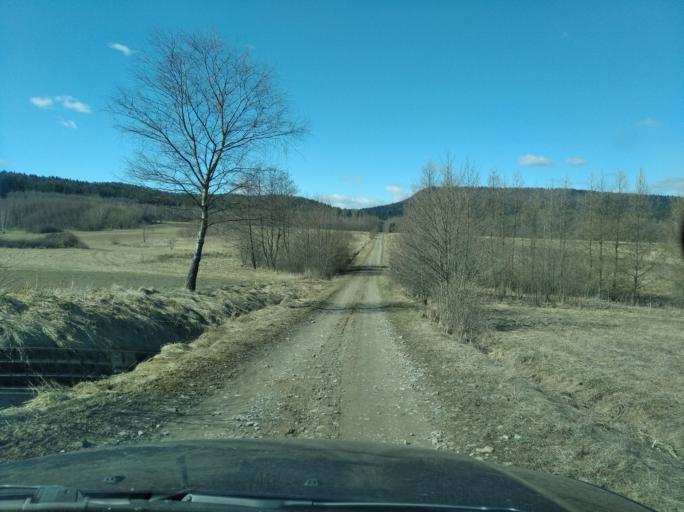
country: PL
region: Subcarpathian Voivodeship
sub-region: Powiat krosnienski
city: Korczyna
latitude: 49.7774
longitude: 21.8438
